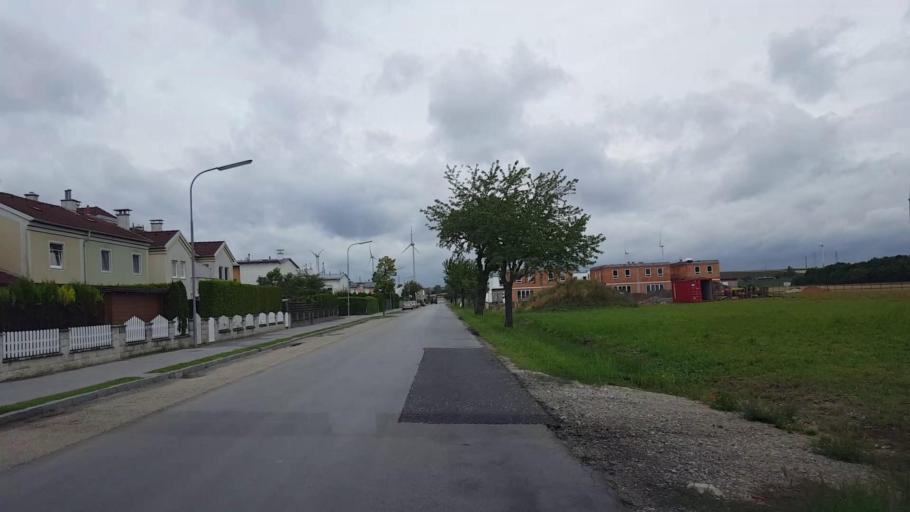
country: AT
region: Lower Austria
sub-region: Politischer Bezirk Bruck an der Leitha
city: Bruck an der Leitha
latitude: 48.0172
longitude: 16.7201
